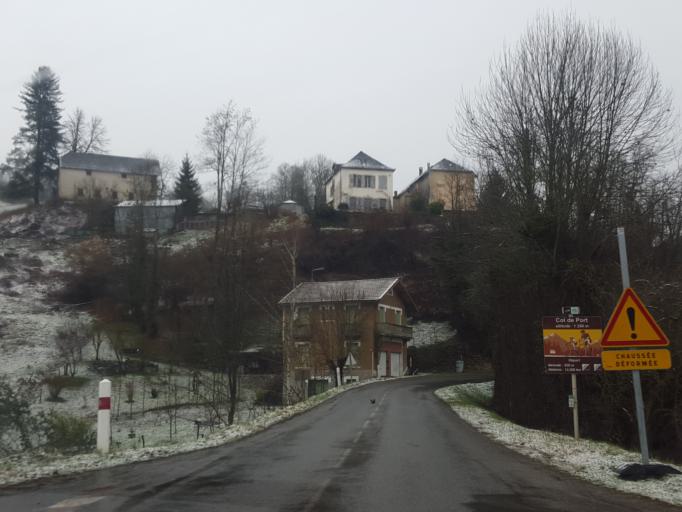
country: FR
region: Midi-Pyrenees
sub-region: Departement de l'Ariege
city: Montjoie-en-Couserans
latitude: 42.8925
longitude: 1.3494
